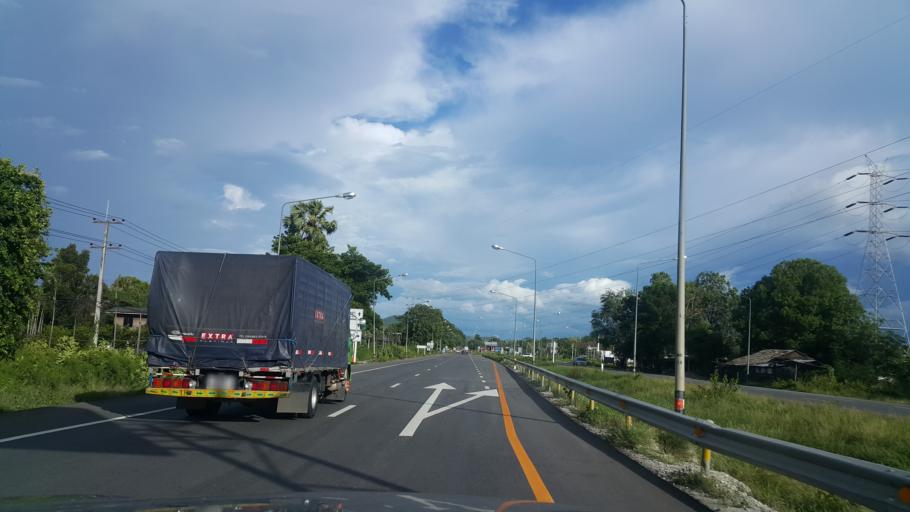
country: TH
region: Tak
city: Ban Tak
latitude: 17.0348
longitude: 99.0884
